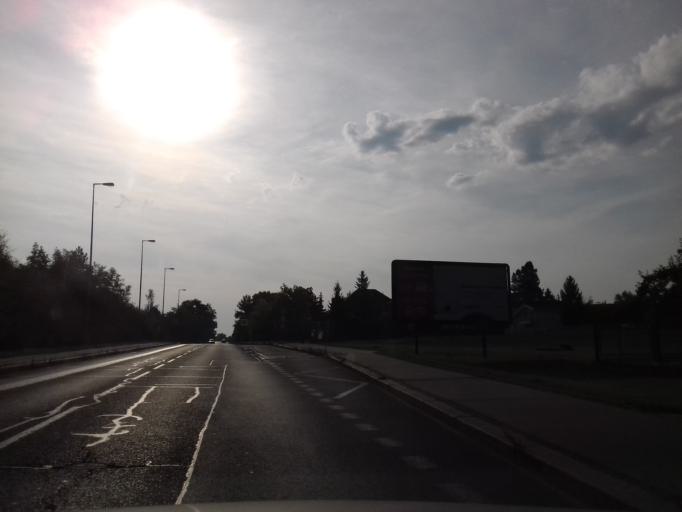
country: CZ
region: Central Bohemia
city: Vestec
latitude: 50.0160
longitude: 14.4695
